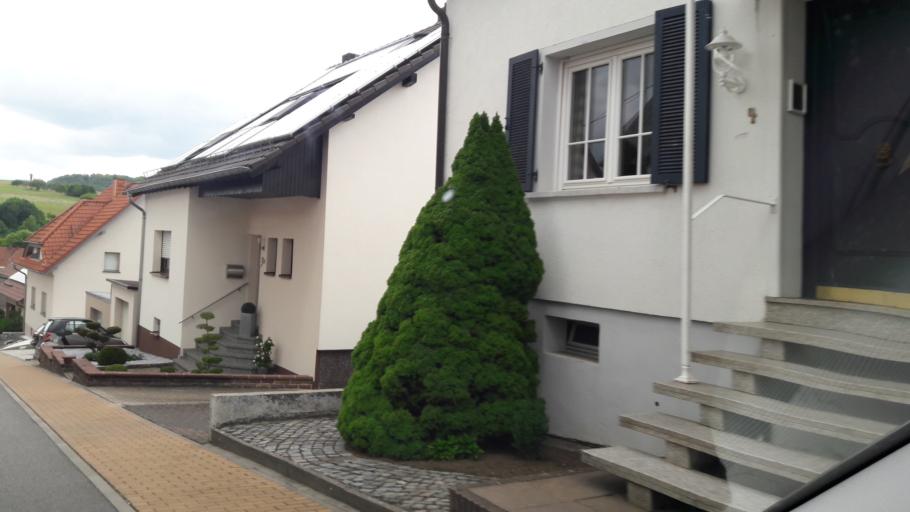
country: DE
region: Saarland
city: Tholey
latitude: 49.4638
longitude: 7.0035
